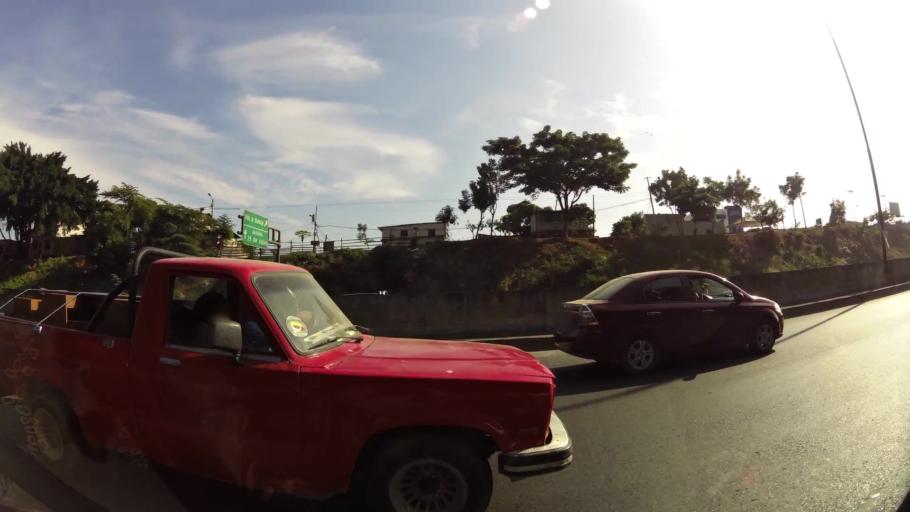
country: EC
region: Guayas
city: Eloy Alfaro
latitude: -2.0793
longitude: -79.9324
